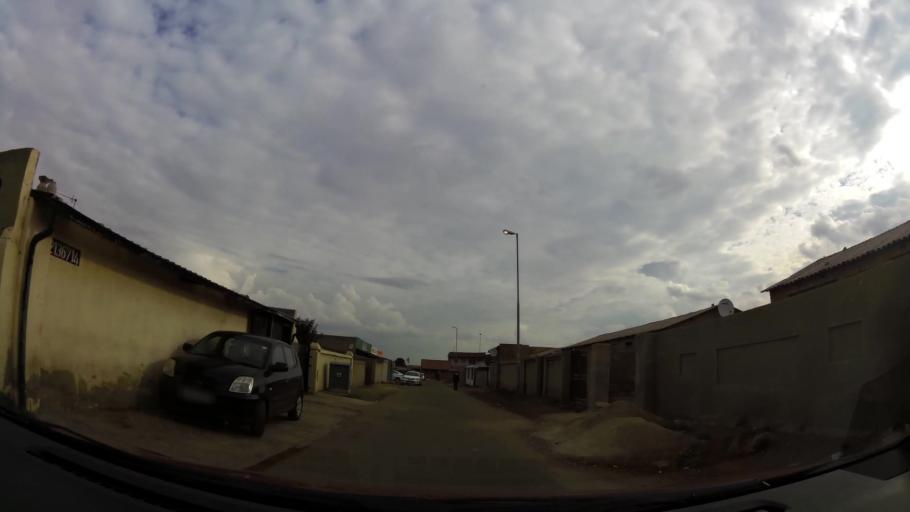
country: ZA
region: Gauteng
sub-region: City of Johannesburg Metropolitan Municipality
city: Soweto
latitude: -26.2460
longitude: 27.8384
